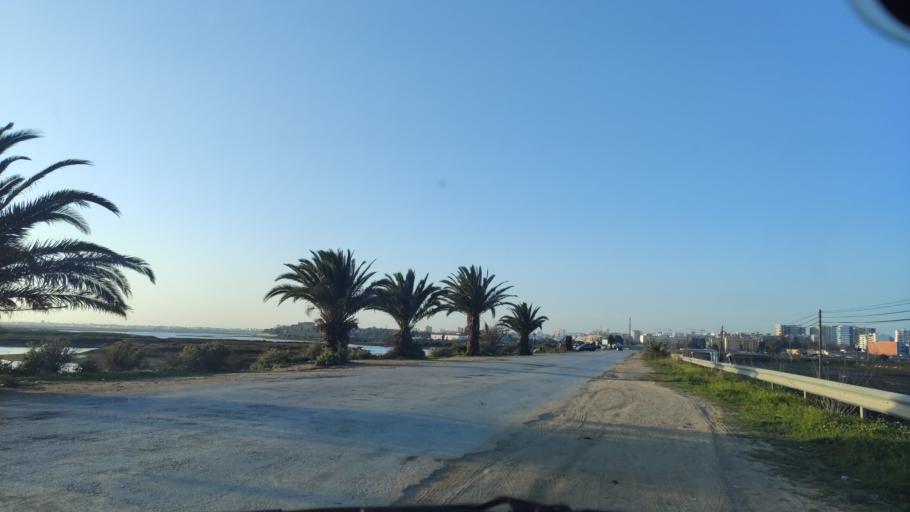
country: PT
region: Faro
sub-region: Faro
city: Faro
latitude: 37.0143
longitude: -7.9224
